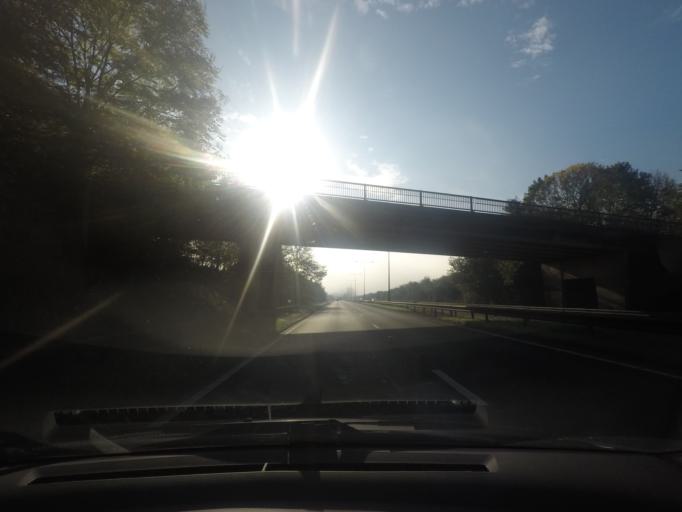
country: GB
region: England
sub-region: East Riding of Yorkshire
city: Welton
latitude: 53.7401
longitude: -0.5638
